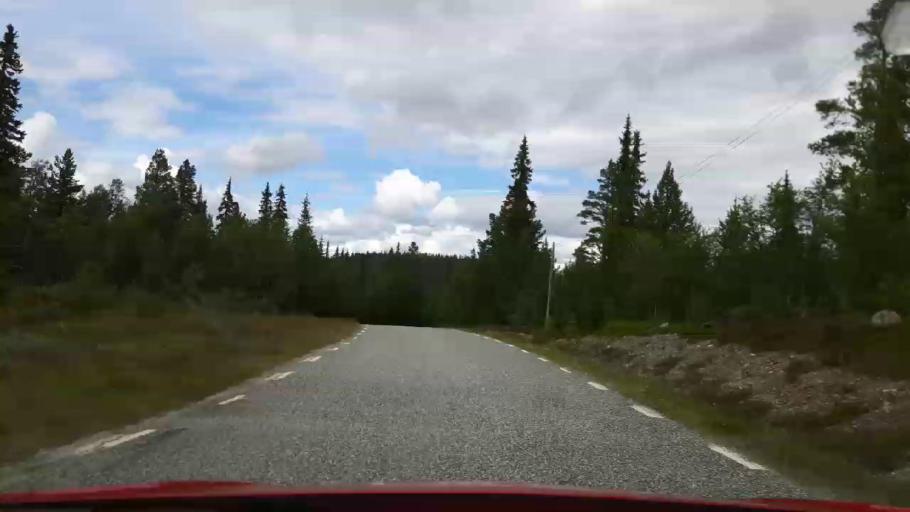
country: NO
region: Hedmark
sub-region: Engerdal
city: Engerdal
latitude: 62.3557
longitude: 12.7941
